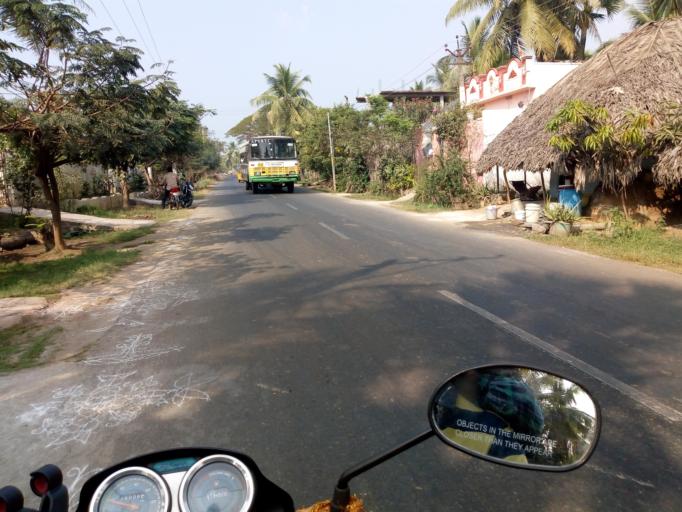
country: IN
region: Andhra Pradesh
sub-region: West Godavari
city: Palakollu
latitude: 16.5901
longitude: 81.6437
